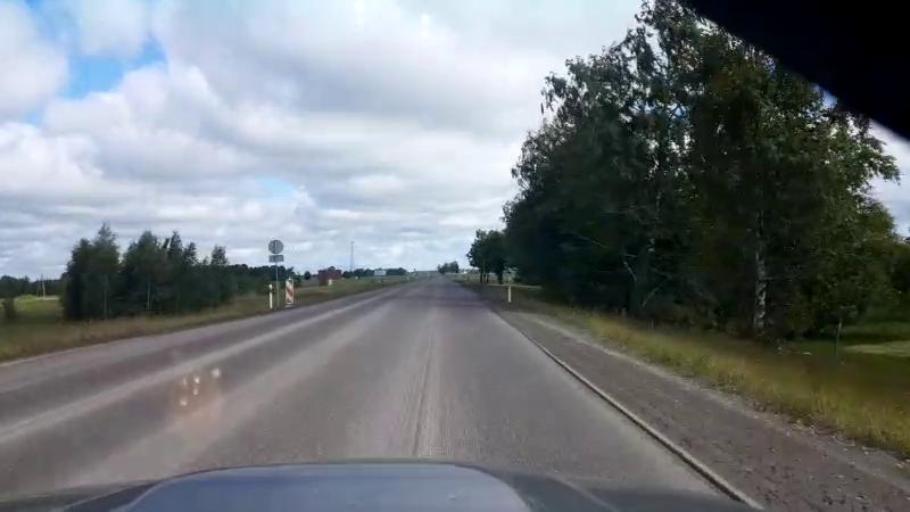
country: LV
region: Bauskas Rajons
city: Bauska
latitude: 56.2841
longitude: 24.3592
